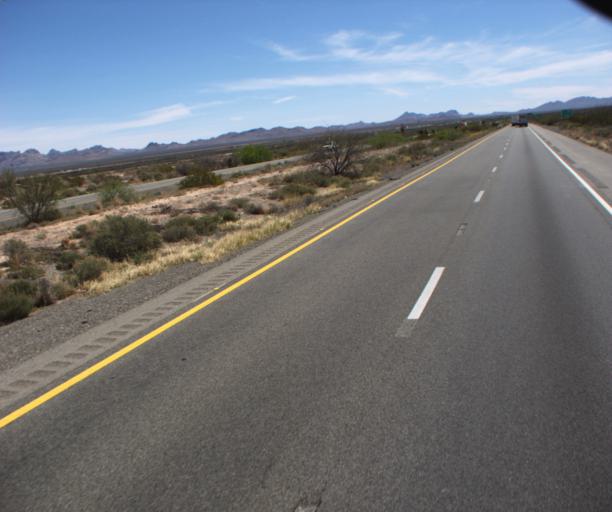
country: US
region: New Mexico
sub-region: Hidalgo County
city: Lordsburg
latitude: 32.2602
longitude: -109.2154
